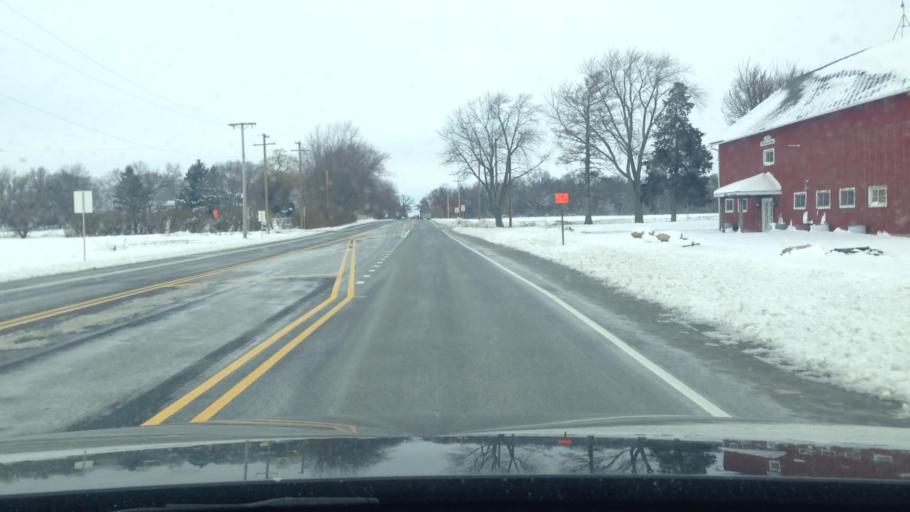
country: US
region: Illinois
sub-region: McHenry County
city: Hebron
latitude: 42.4134
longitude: -88.4381
